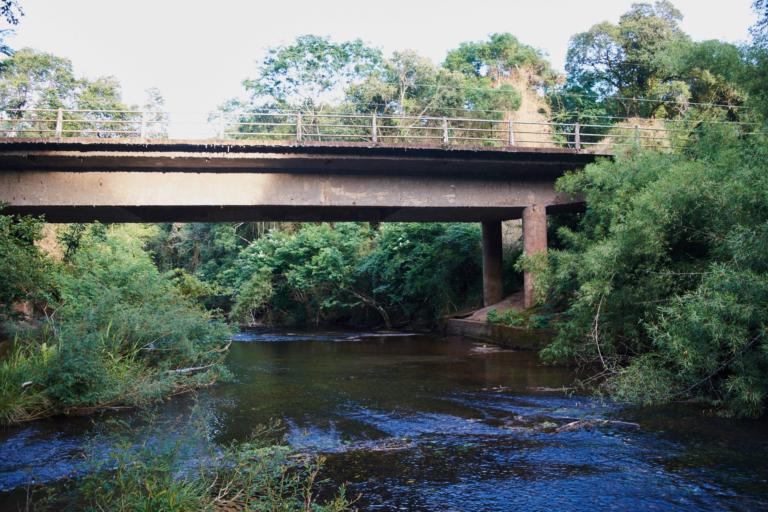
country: AR
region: Misiones
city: Colonia Wanda
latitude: -25.8579
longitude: -54.1683
